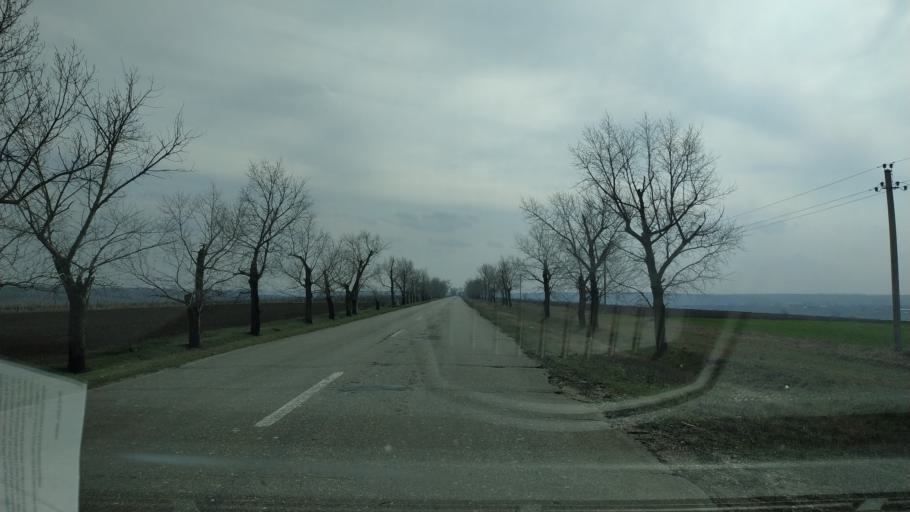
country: MD
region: Gagauzia
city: Vulcanesti
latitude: 45.7112
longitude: 28.4003
